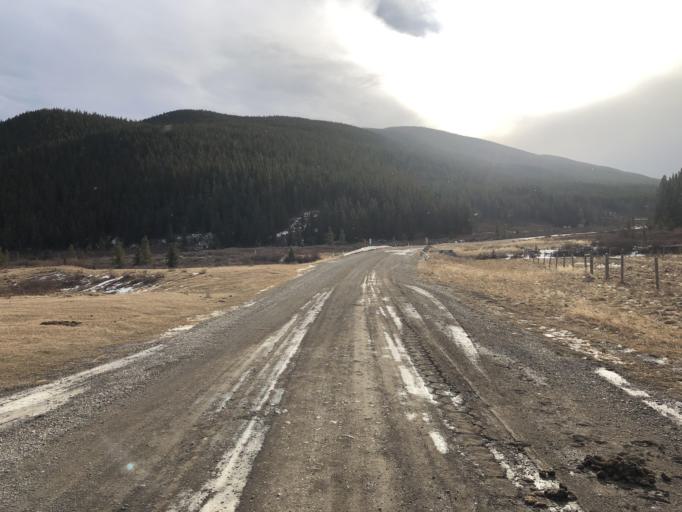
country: CA
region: Alberta
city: Canmore
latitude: 50.8786
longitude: -114.8906
